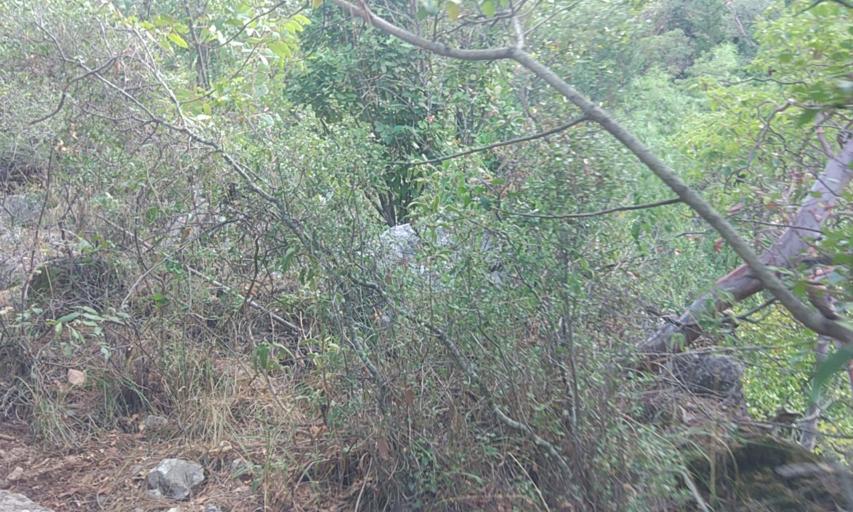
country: TR
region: Antalya
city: Tekirova
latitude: 36.3818
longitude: 30.4754
